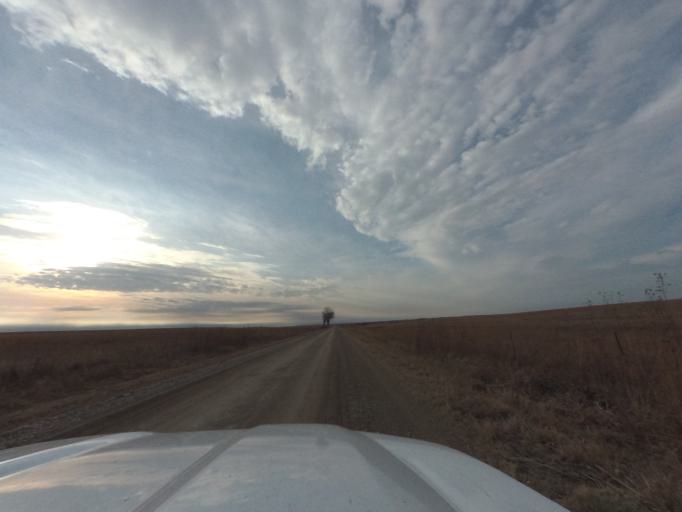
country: US
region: Kansas
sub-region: Morris County
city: Council Grove
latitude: 38.5021
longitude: -96.4102
